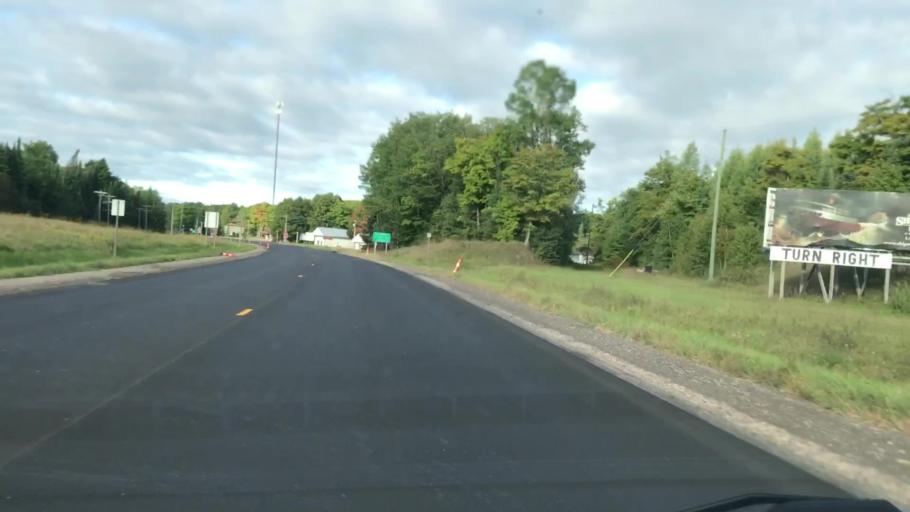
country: US
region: Michigan
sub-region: Luce County
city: Newberry
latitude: 46.3463
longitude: -85.0273
